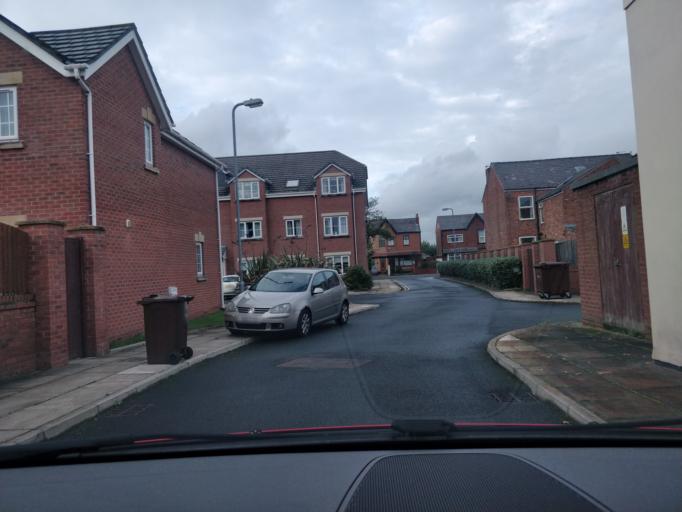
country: GB
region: England
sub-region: Sefton
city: Southport
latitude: 53.6427
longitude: -2.9797
